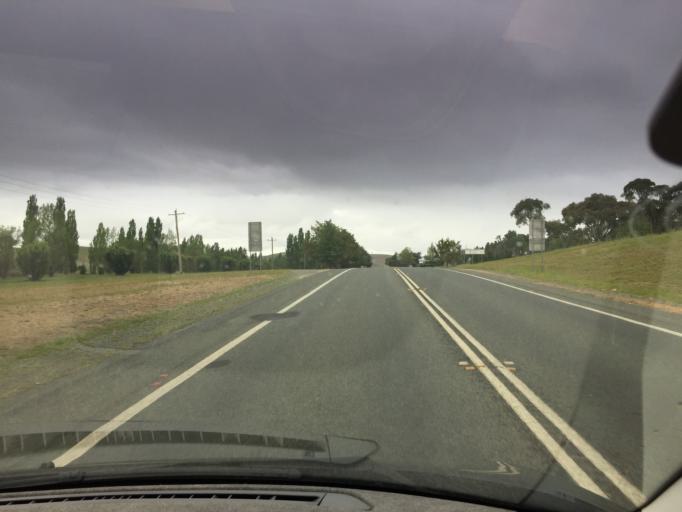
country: AU
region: New South Wales
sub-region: Cooma-Monaro
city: Cooma
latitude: -36.2216
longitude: 149.1336
